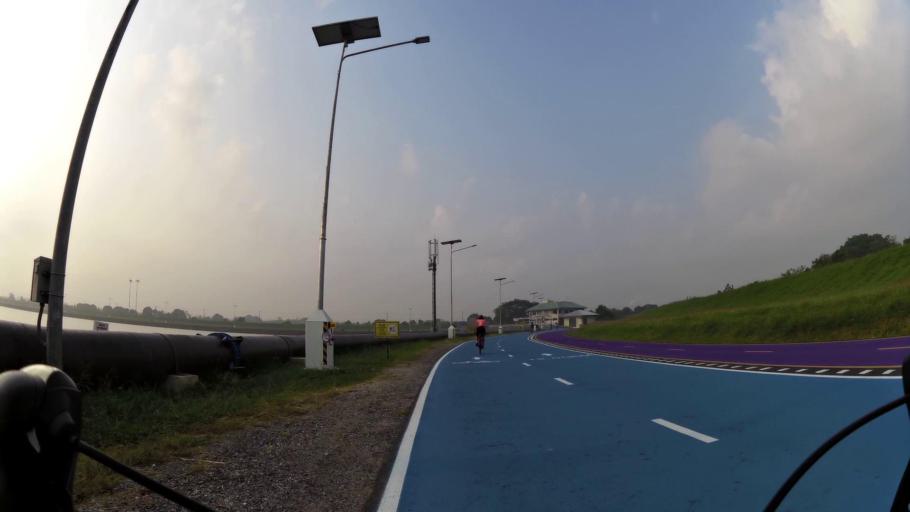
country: TH
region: Bangkok
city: Lat Krabang
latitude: 13.6944
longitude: 100.7733
